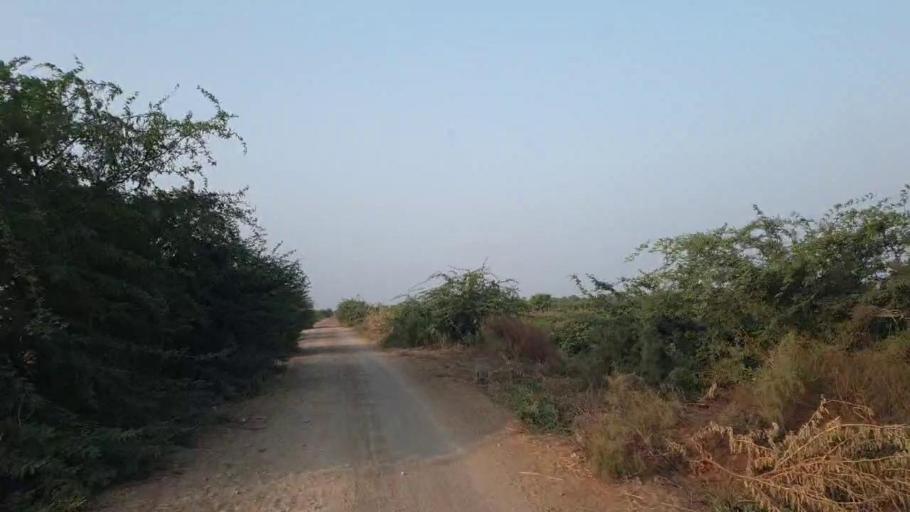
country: PK
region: Sindh
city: Tando Ghulam Ali
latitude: 25.0557
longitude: 68.9604
